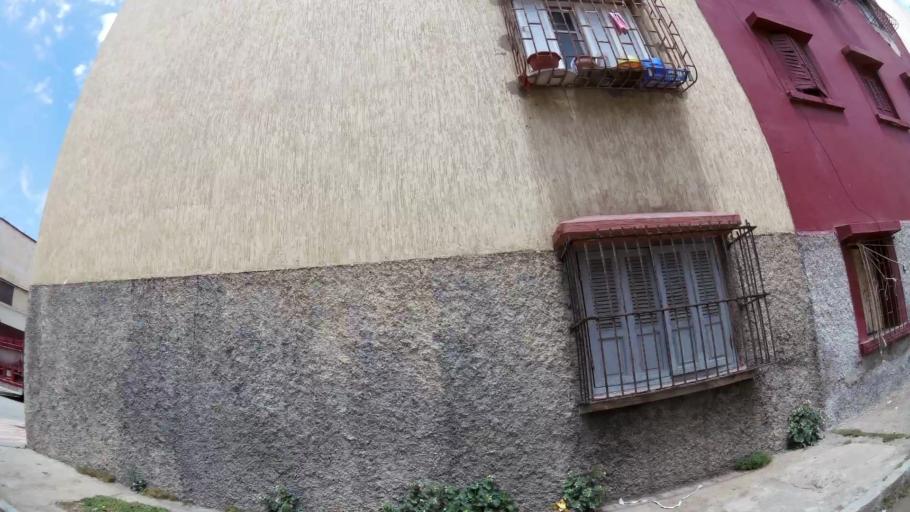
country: MA
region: Rabat-Sale-Zemmour-Zaer
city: Sale
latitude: 34.0478
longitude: -6.8269
